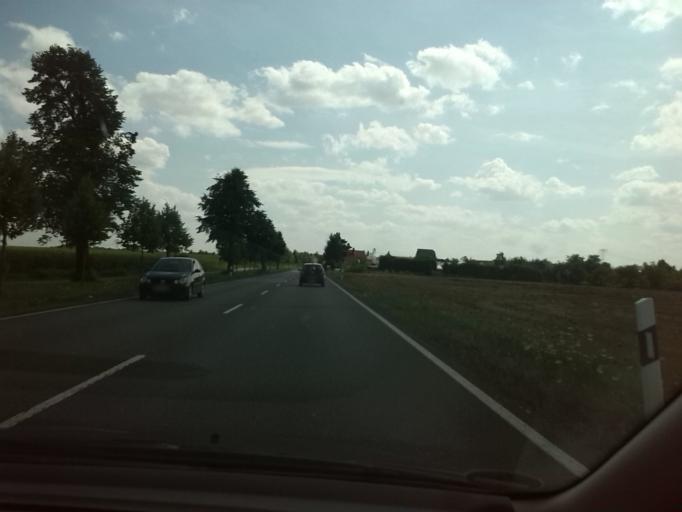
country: DE
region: Thuringia
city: Fockendorf
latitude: 51.0311
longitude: 12.4580
